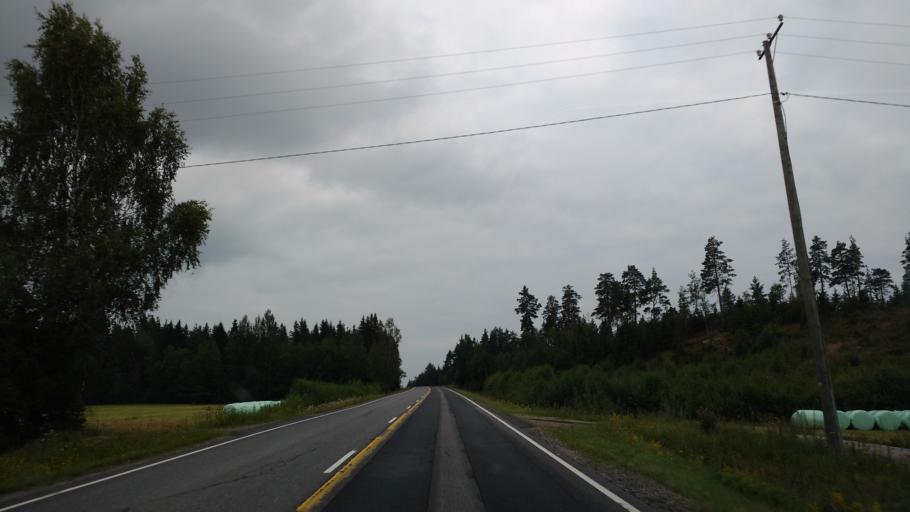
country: FI
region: Varsinais-Suomi
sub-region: Salo
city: Halikko
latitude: 60.4666
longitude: 23.0170
